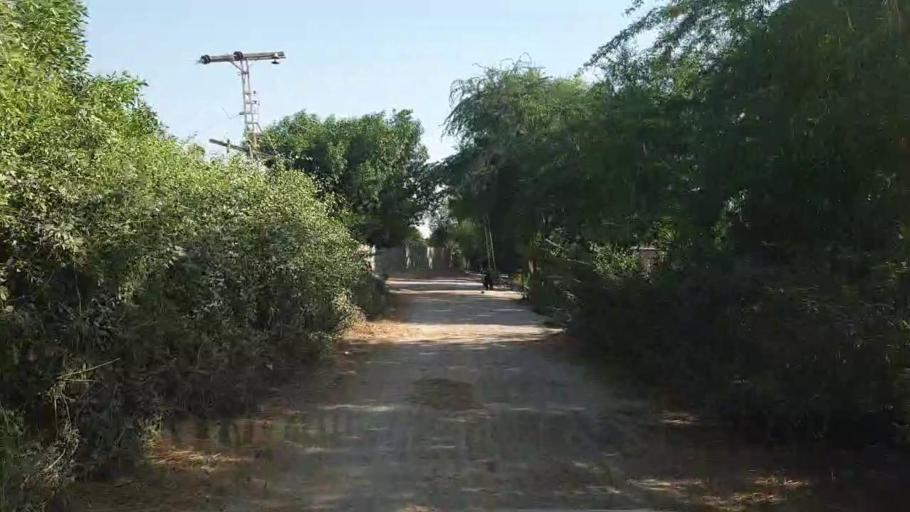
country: PK
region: Sindh
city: Matli
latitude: 25.0272
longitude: 68.7329
